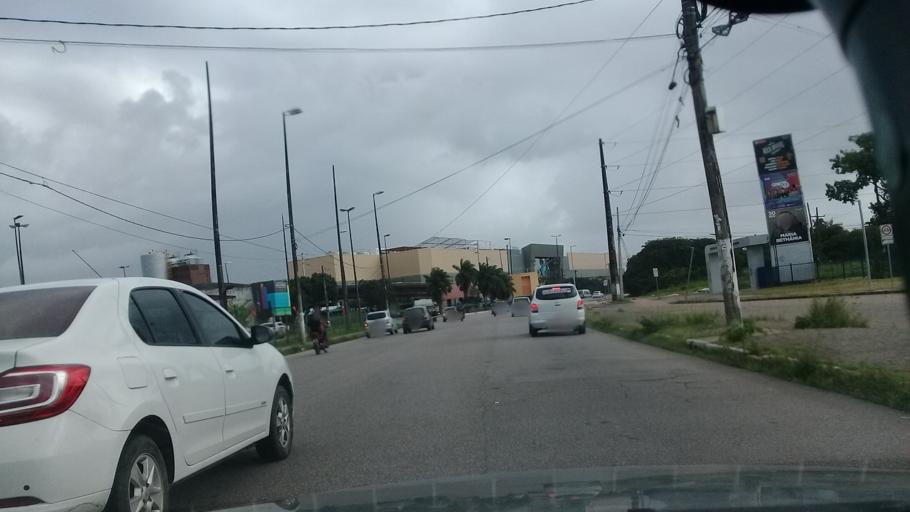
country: BR
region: Pernambuco
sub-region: Recife
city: Recife
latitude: -8.0350
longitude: -34.8702
